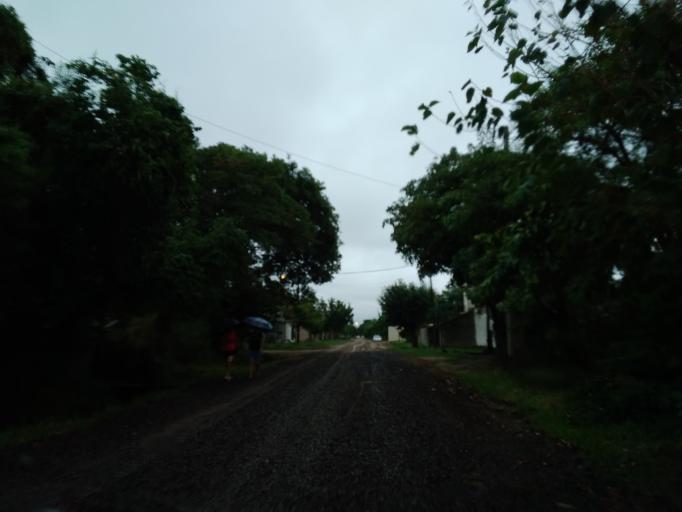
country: AR
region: Corrientes
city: Corrientes
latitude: -27.4893
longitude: -58.8196
